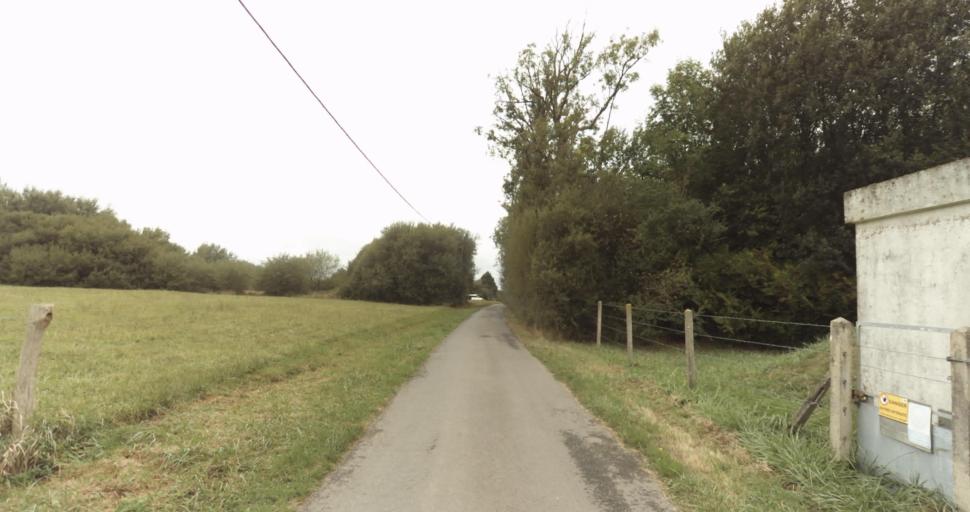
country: FR
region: Lower Normandy
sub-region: Departement de l'Orne
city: Sainte-Gauburge-Sainte-Colombe
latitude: 48.7108
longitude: 0.4414
